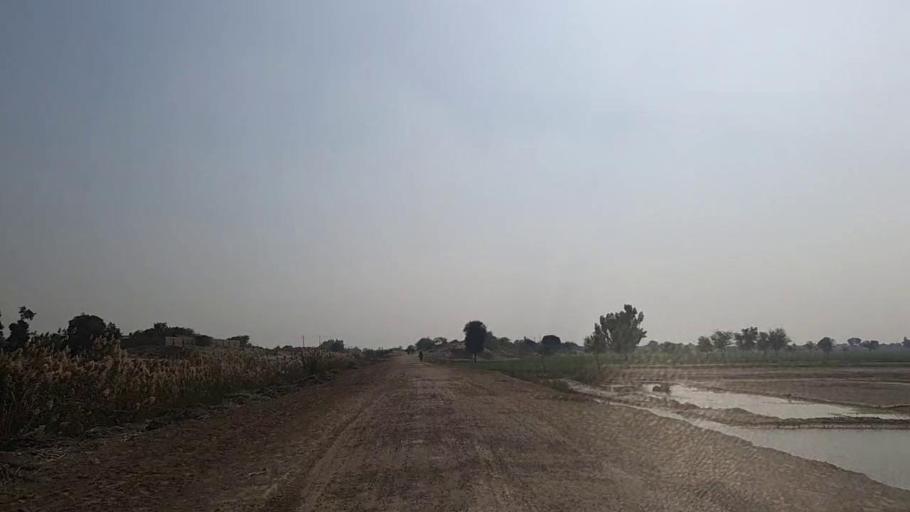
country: PK
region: Sindh
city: Daur
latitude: 26.4679
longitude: 68.4667
